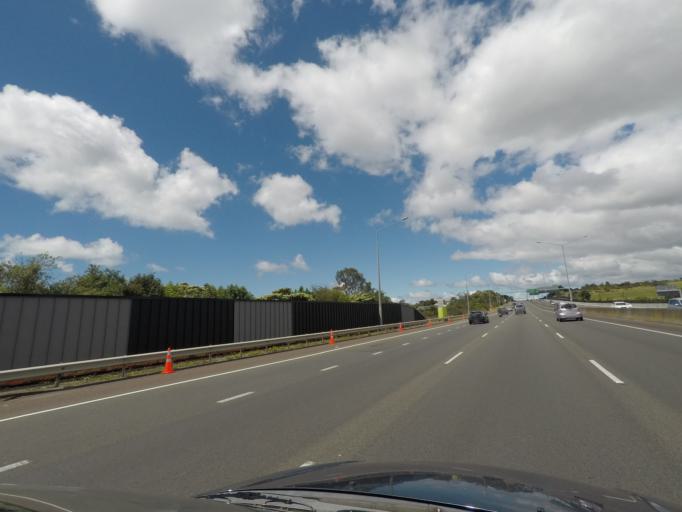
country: NZ
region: Auckland
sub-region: Auckland
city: Rosebank
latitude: -36.8243
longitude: 174.6169
